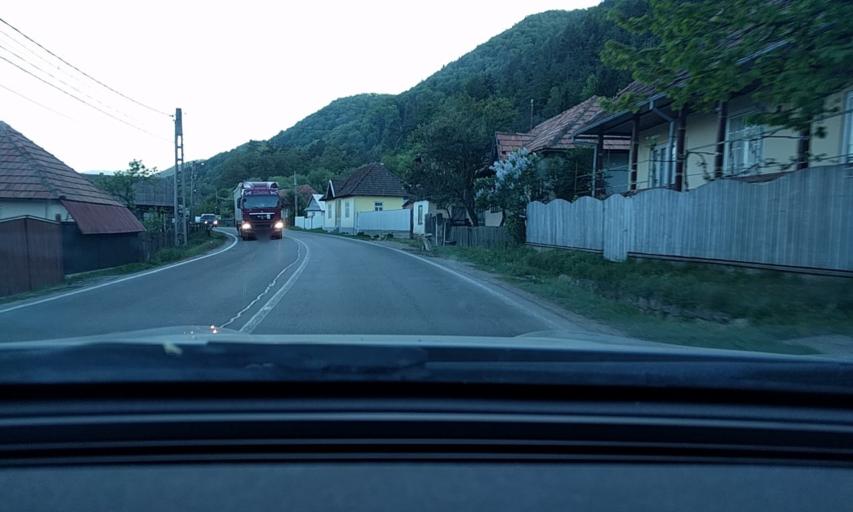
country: RO
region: Bacau
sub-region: Oras Slanic-Moldova
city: Slanic-Moldova
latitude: 46.1639
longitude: 26.4658
